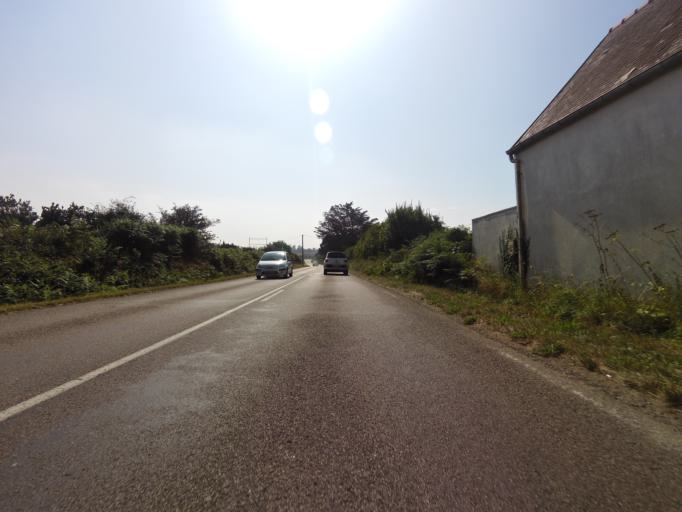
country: FR
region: Brittany
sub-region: Departement du Finistere
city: Plozevet
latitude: 47.9998
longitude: -4.4433
